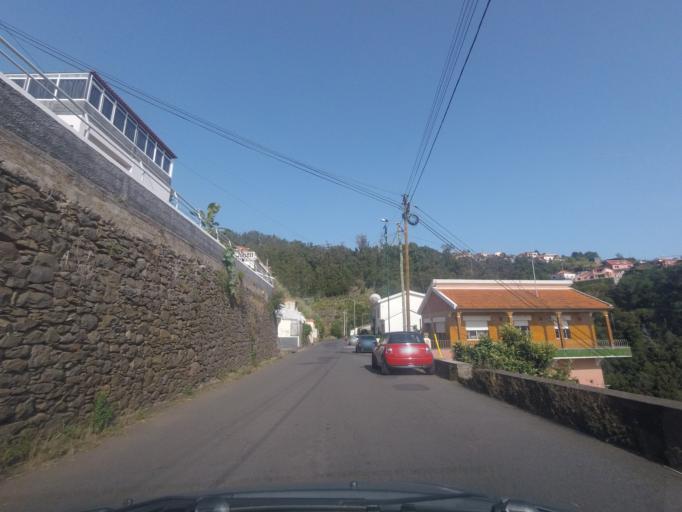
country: PT
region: Madeira
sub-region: Calheta
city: Arco da Calheta
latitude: 32.7261
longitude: -17.1536
